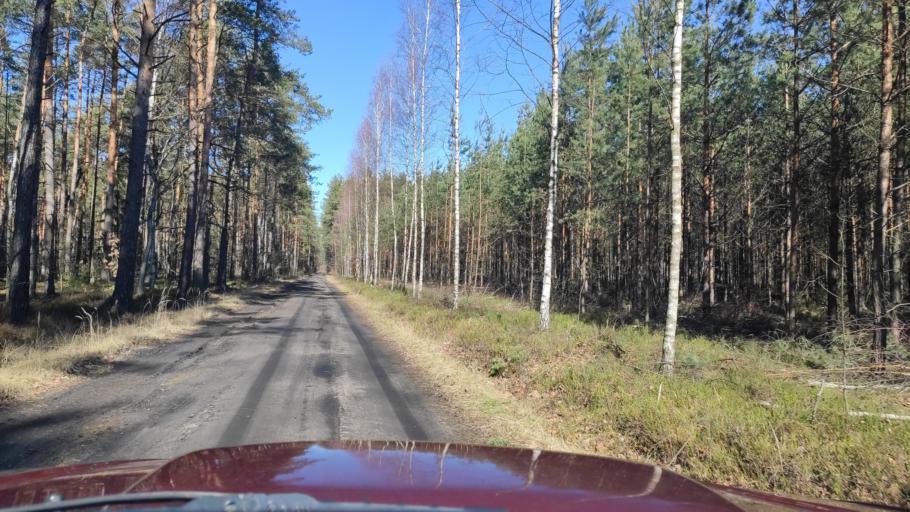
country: PL
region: Masovian Voivodeship
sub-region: Powiat kozienicki
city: Garbatka-Letnisko
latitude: 51.4296
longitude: 21.5487
